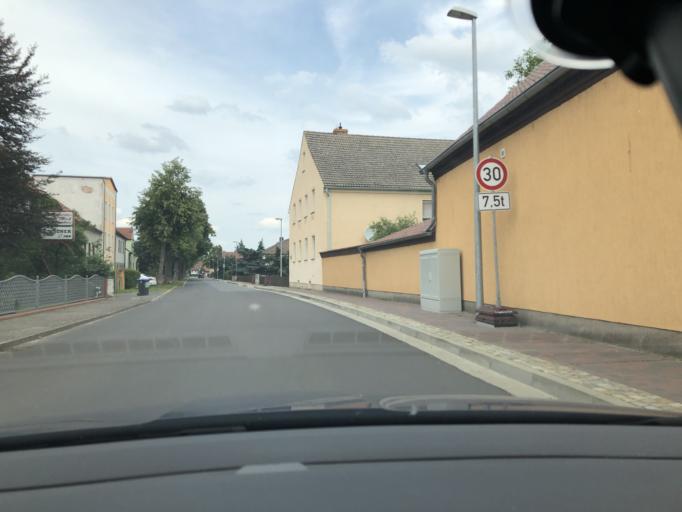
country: DE
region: Brandenburg
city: Kasel-Golzig
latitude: 51.9787
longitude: 13.7654
